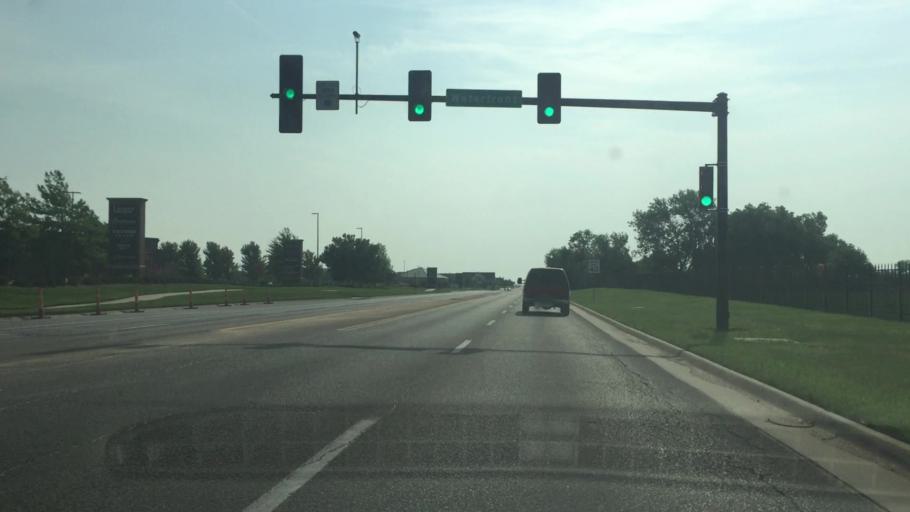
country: US
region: Kansas
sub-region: Sedgwick County
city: Bellaire
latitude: 37.7084
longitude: -97.2224
